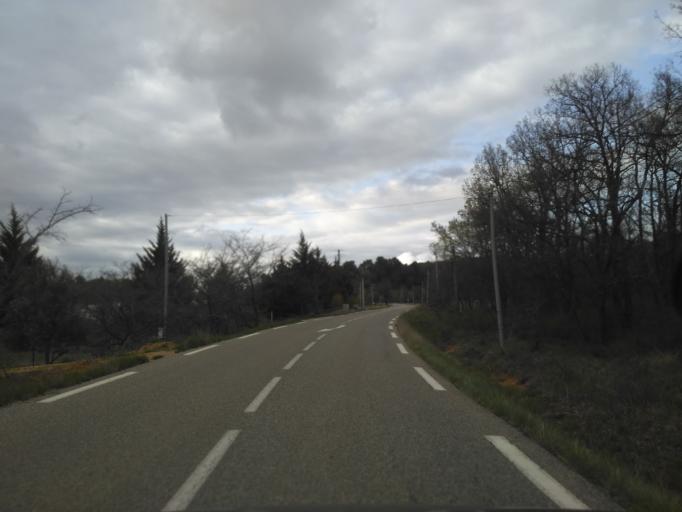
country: FR
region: Provence-Alpes-Cote d'Azur
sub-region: Departement du Var
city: Barjols
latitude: 43.6162
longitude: 5.9472
